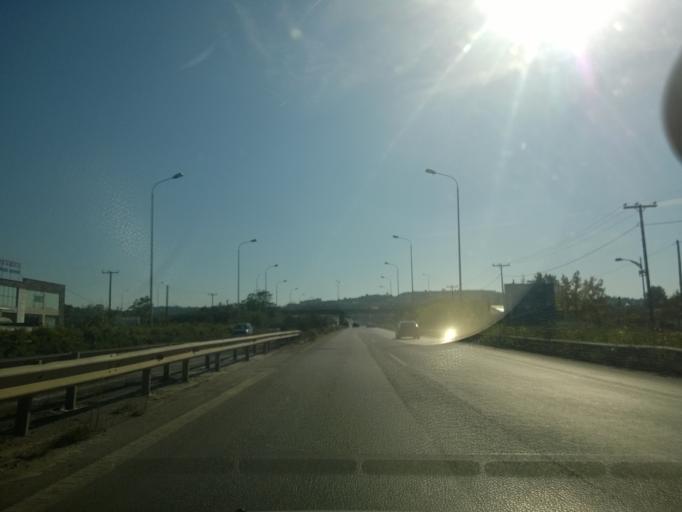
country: GR
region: Central Macedonia
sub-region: Nomos Thessalonikis
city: Neo Rysi
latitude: 40.4978
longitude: 23.0029
